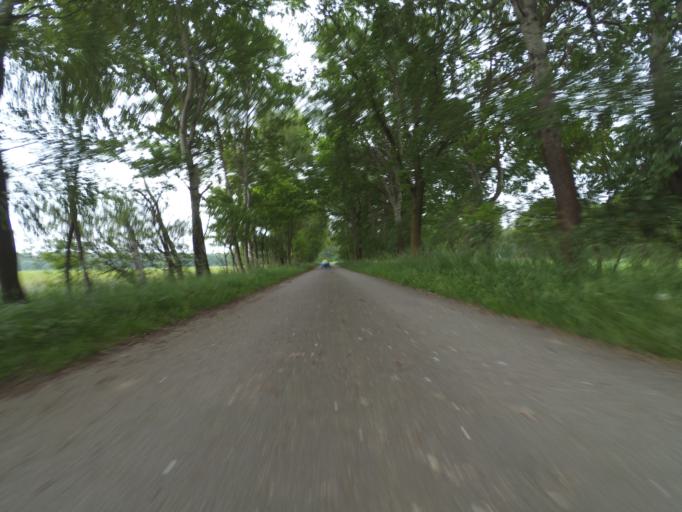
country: DE
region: Lower Saxony
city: Edemissen
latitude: 52.3736
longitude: 10.3151
